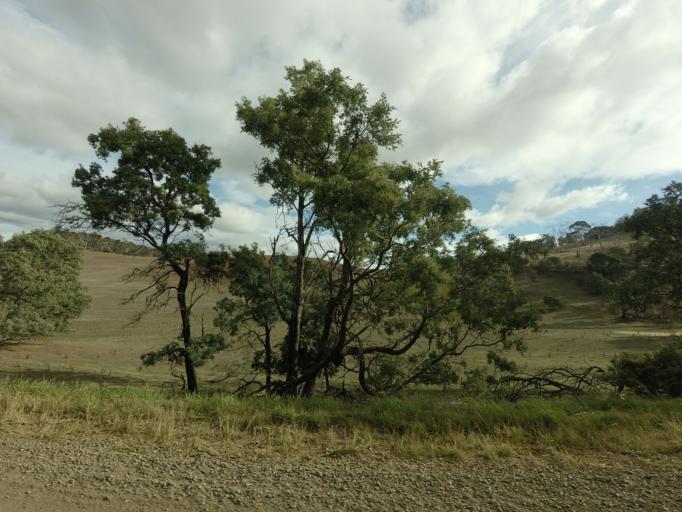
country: AU
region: Tasmania
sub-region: Brighton
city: Bridgewater
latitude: -42.4607
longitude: 147.2714
